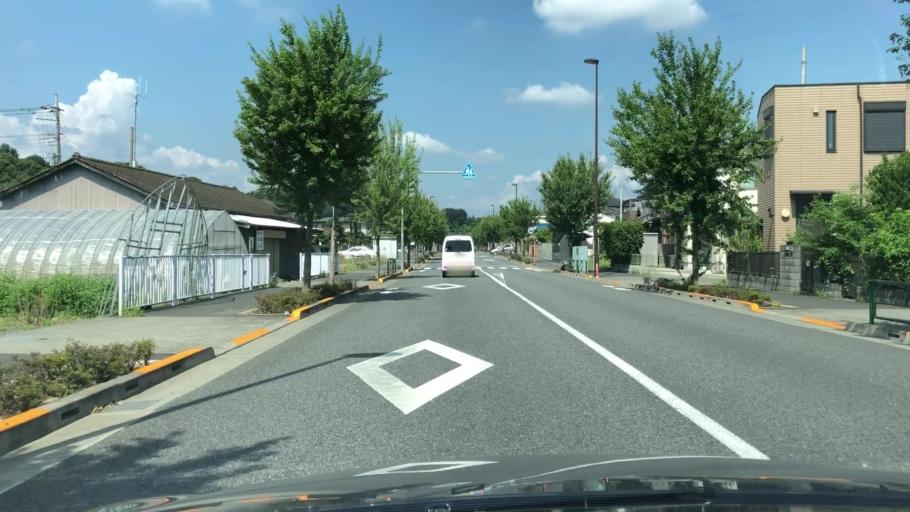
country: JP
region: Tokyo
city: Hino
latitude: 35.6844
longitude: 139.3858
